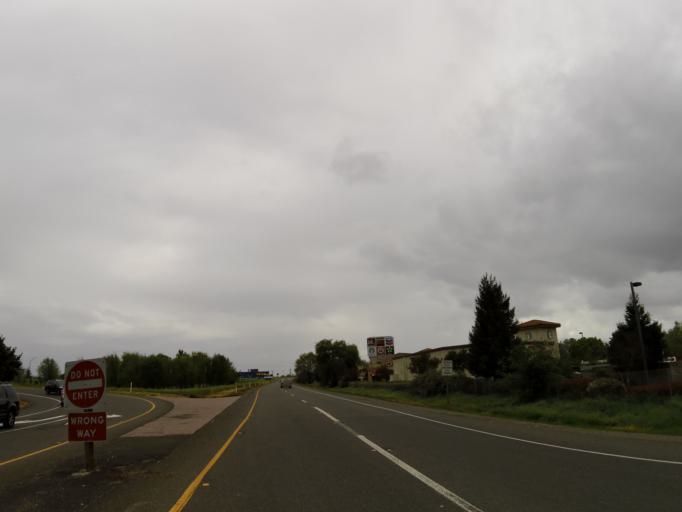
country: US
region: California
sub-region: Yolo County
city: West Sacramento
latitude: 38.5920
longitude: -121.5541
